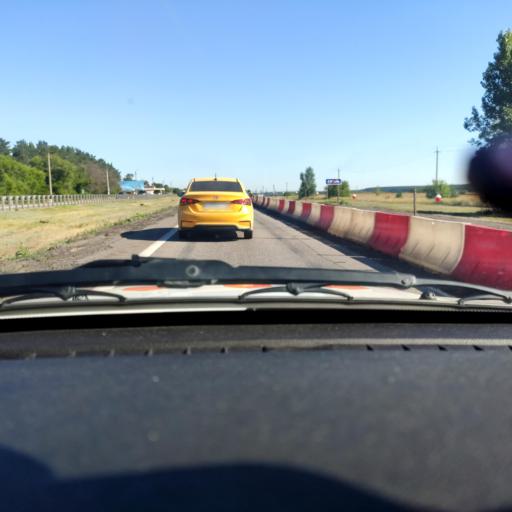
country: RU
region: Voronezj
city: Ramon'
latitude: 52.0398
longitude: 39.1983
